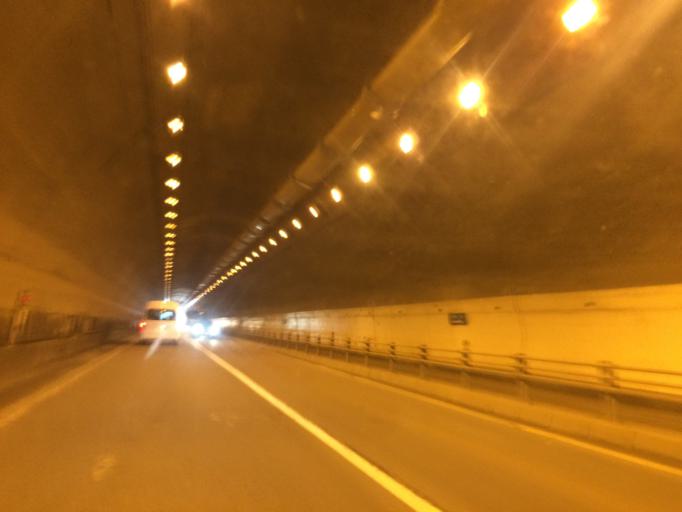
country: JP
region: Hokkaido
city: Otaru
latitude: 43.2095
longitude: 140.9031
